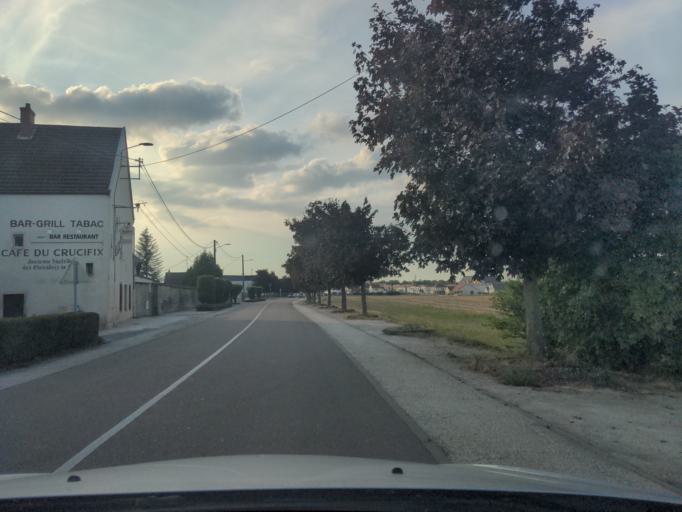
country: FR
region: Bourgogne
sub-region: Departement de la Cote-d'Or
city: Neuilly-les-Dijon
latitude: 47.2751
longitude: 5.1205
